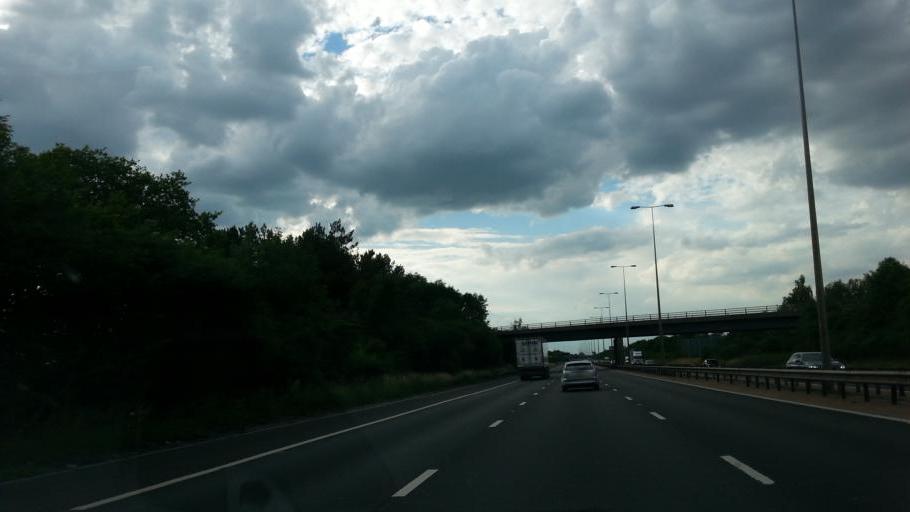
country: GB
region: England
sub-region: Worcestershire
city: Upton upon Severn
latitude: 52.0755
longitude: -2.1664
